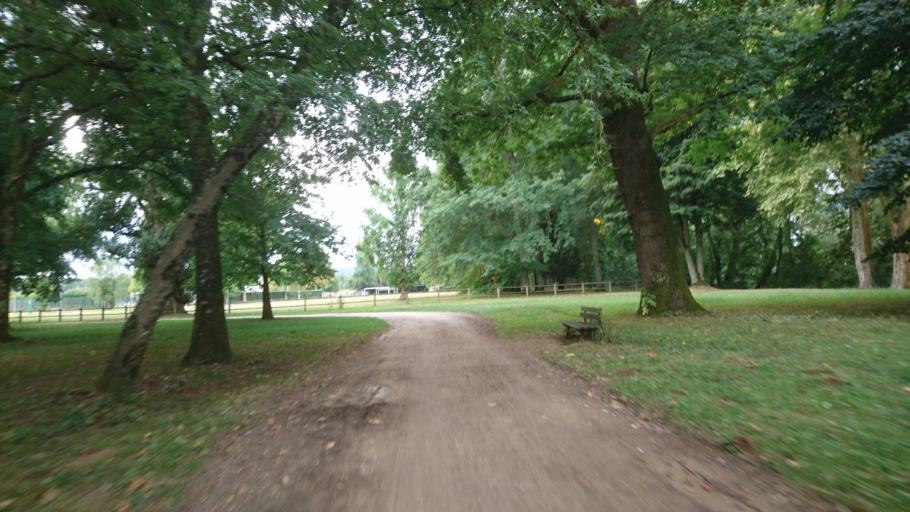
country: FR
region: Limousin
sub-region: Departement de la Correze
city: Ussac
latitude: 45.1609
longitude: 1.4914
